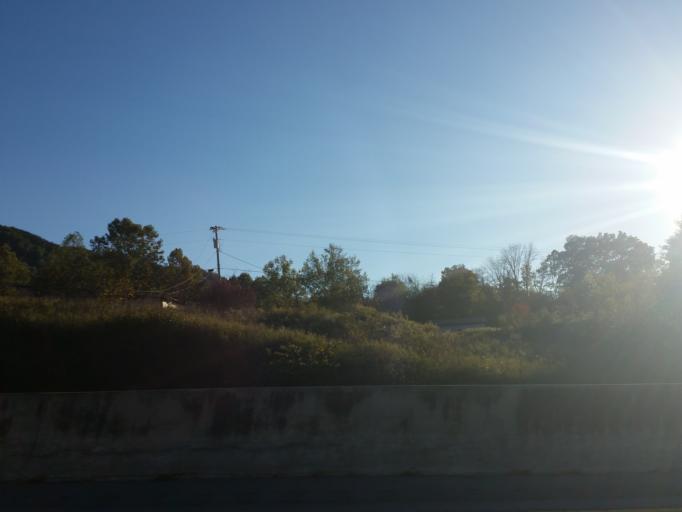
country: US
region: Tennessee
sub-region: Grainger County
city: Rutledge
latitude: 36.3483
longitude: -83.4317
